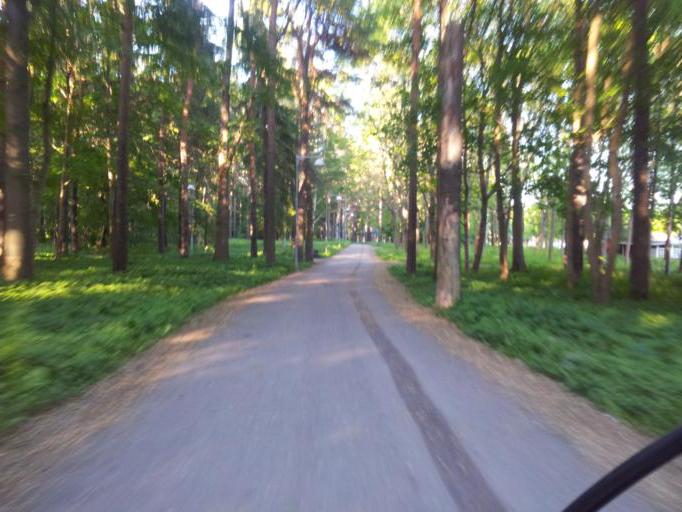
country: SE
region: Uppsala
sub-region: Uppsala Kommun
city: Uppsala
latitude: 59.8788
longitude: 17.6415
